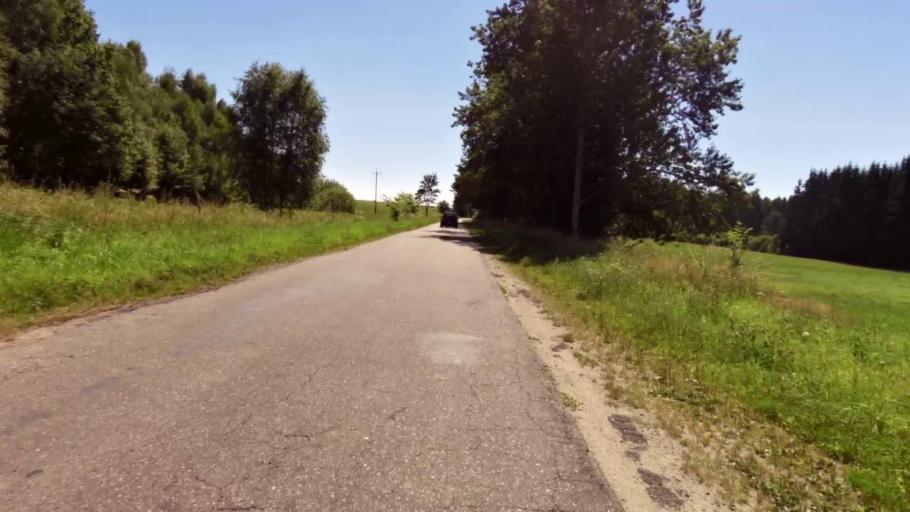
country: PL
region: West Pomeranian Voivodeship
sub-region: Powiat szczecinecki
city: Bialy Bor
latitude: 53.9358
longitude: 16.8536
